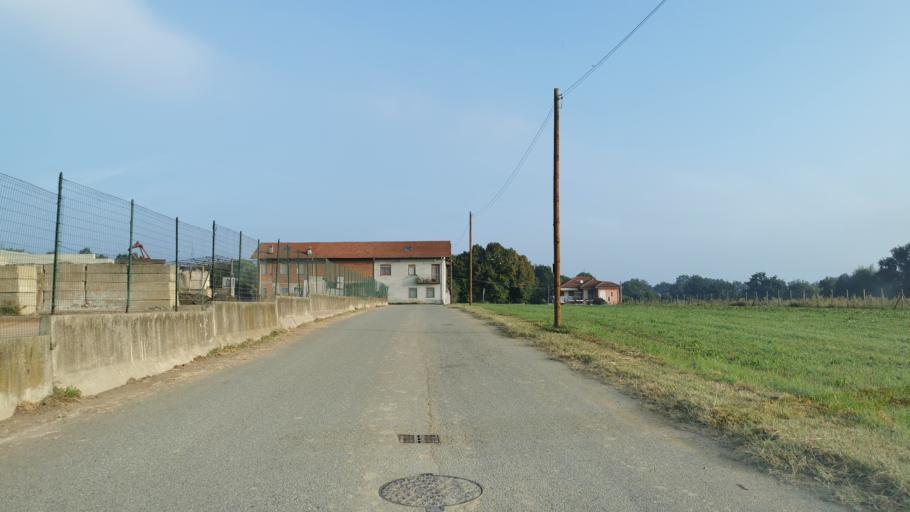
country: IT
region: Piedmont
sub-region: Provincia di Torino
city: Front
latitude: 45.2577
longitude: 7.6623
